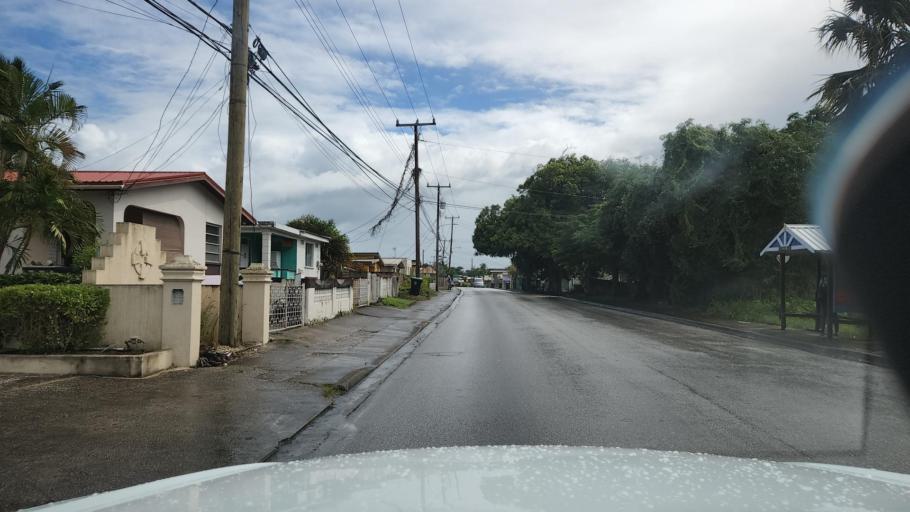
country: BB
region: Saint Michael
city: Bridgetown
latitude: 13.0868
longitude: -59.5760
